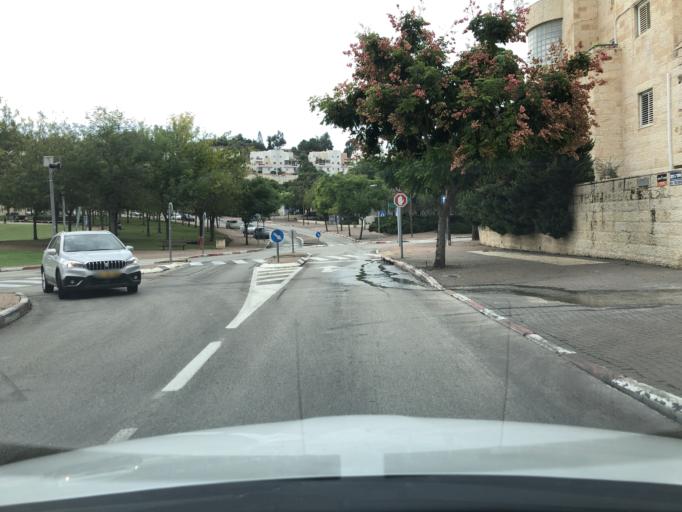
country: IL
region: Central District
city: Modiin
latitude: 31.8972
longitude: 35.0157
